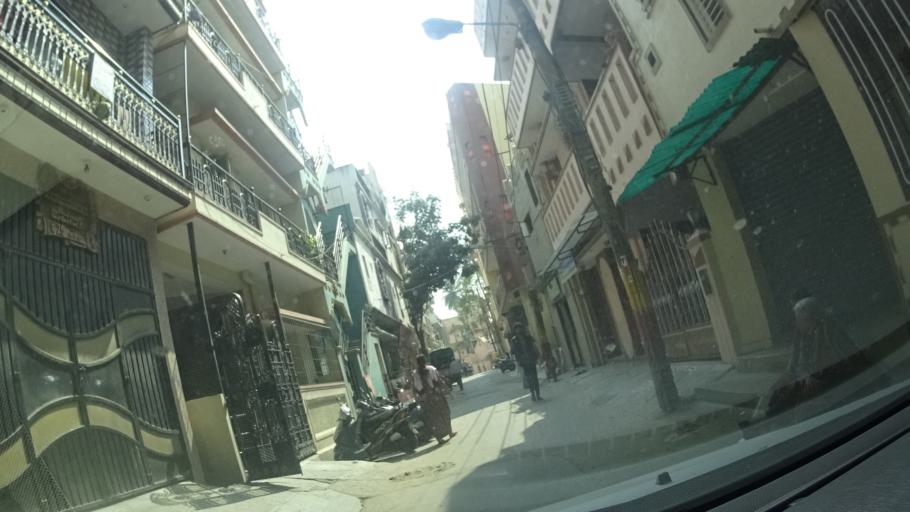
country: IN
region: Karnataka
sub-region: Bangalore Urban
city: Bangalore
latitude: 12.9584
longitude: 77.5575
